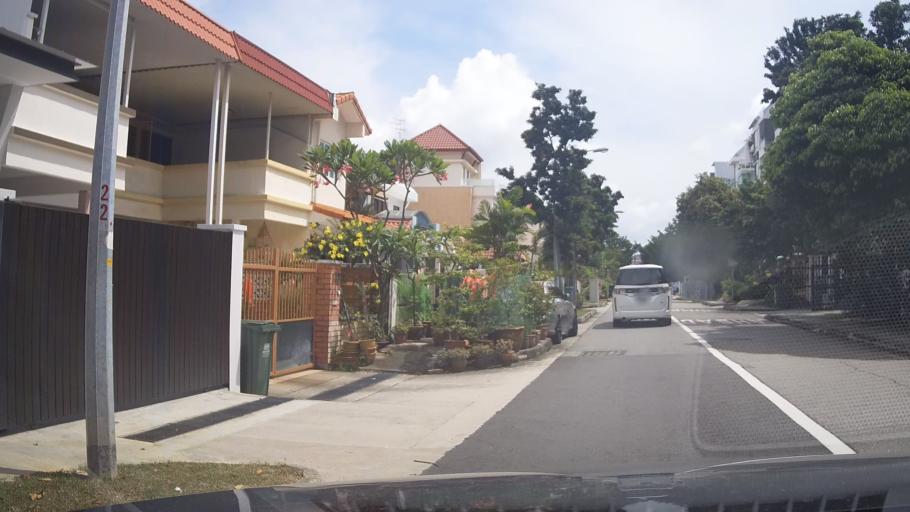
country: SG
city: Singapore
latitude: 1.3149
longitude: 103.9036
